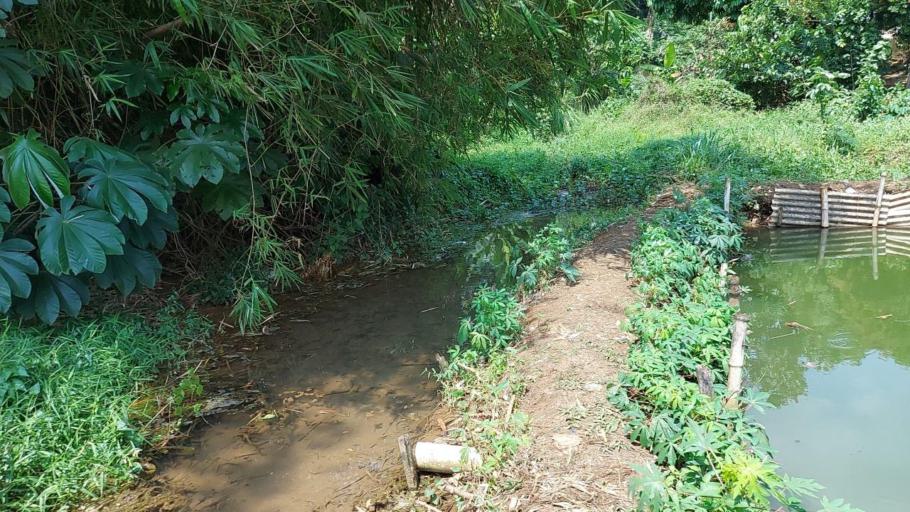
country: ID
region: West Java
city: Cibinong
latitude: -6.4716
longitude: 106.8468
